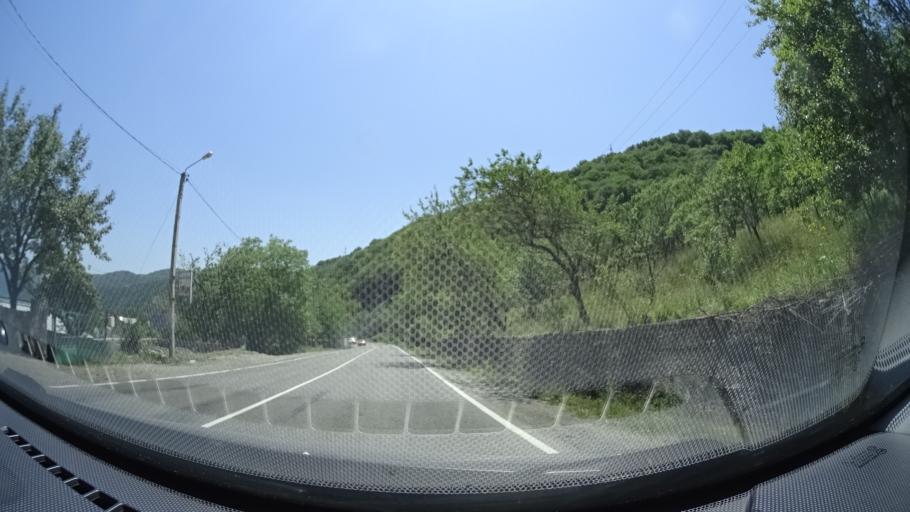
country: GE
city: Zhinvali
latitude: 42.1707
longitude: 44.6947
